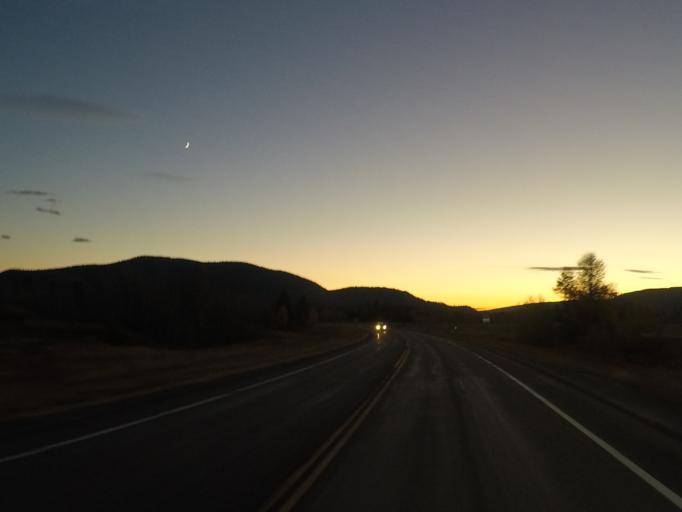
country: US
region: Montana
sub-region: Missoula County
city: Seeley Lake
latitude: 47.0406
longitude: -113.2219
